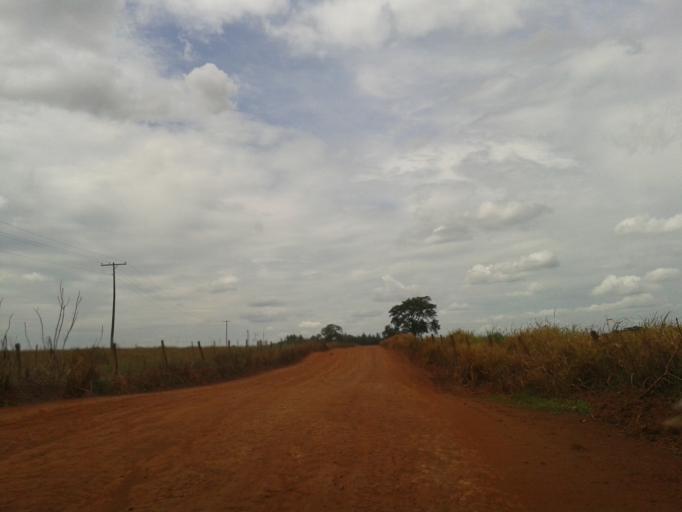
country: BR
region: Minas Gerais
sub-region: Centralina
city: Centralina
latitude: -18.7660
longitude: -49.2428
